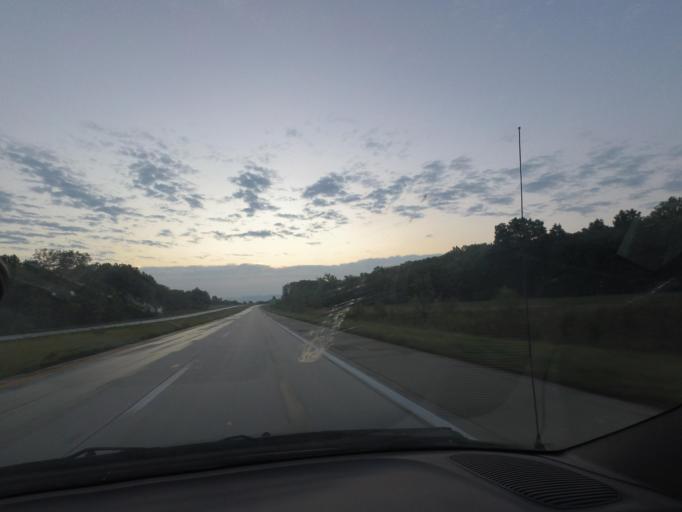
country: US
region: Missouri
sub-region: Macon County
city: Macon
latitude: 39.7599
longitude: -92.5879
